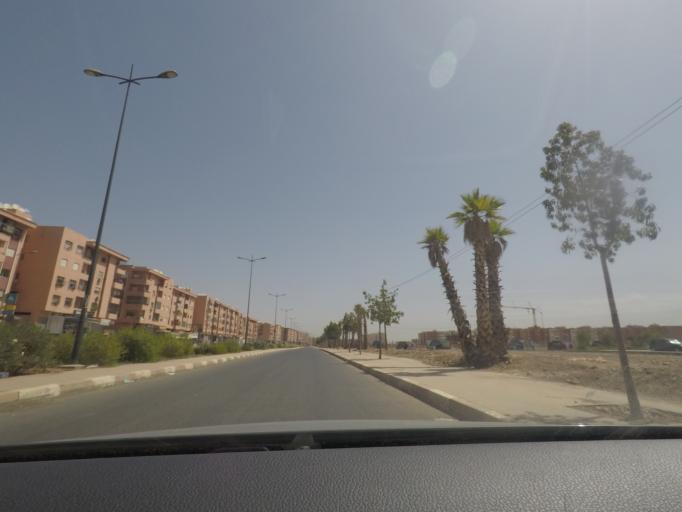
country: MA
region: Marrakech-Tensift-Al Haouz
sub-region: Marrakech
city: Marrakesh
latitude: 31.5859
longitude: -8.0433
